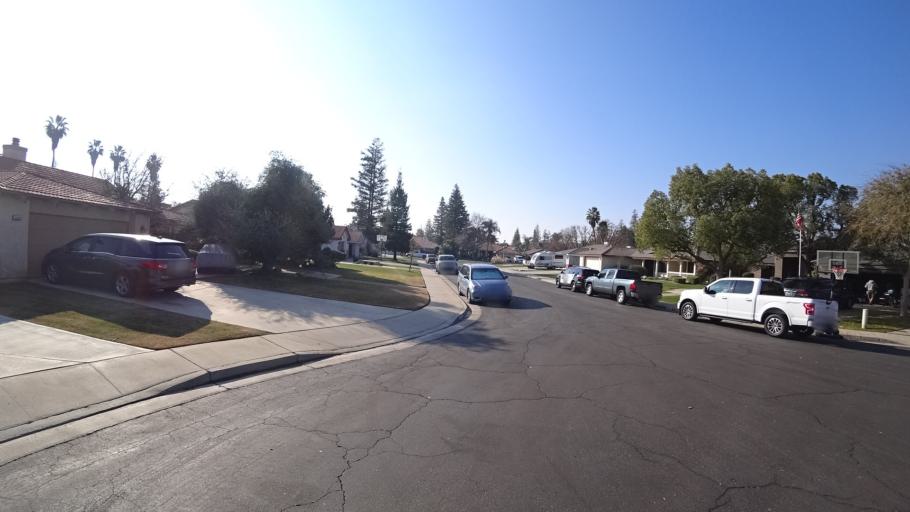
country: US
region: California
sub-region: Kern County
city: Greenacres
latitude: 35.3365
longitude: -119.1102
